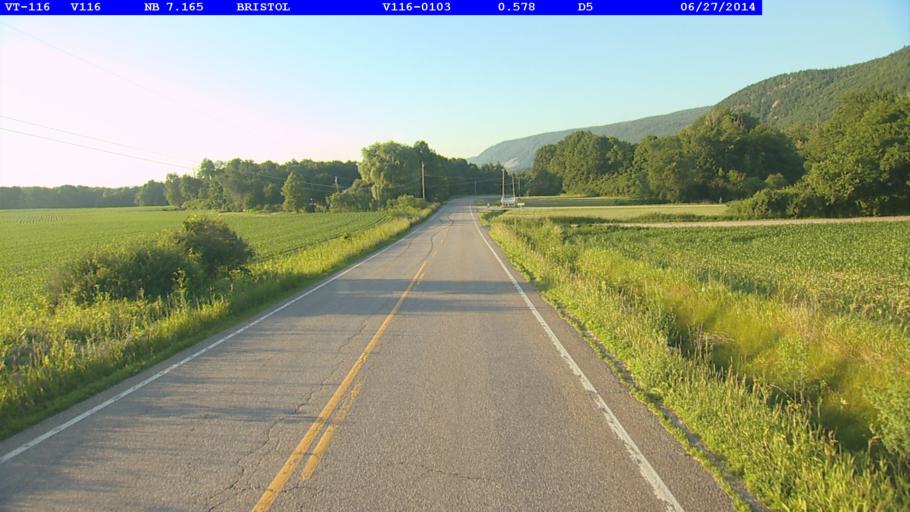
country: US
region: Vermont
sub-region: Addison County
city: Bristol
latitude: 44.0628
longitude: -73.0901
